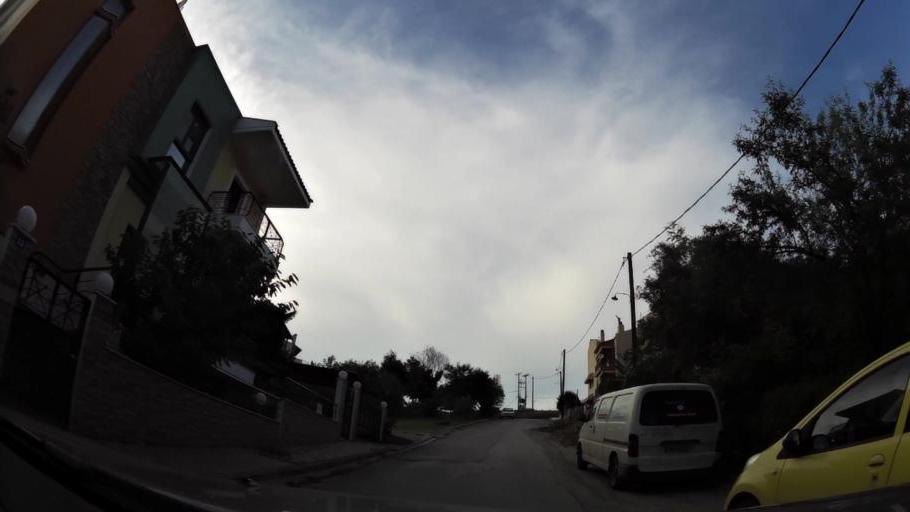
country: GR
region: Central Macedonia
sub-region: Nomos Thessalonikis
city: Pefka
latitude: 40.6537
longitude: 22.9997
